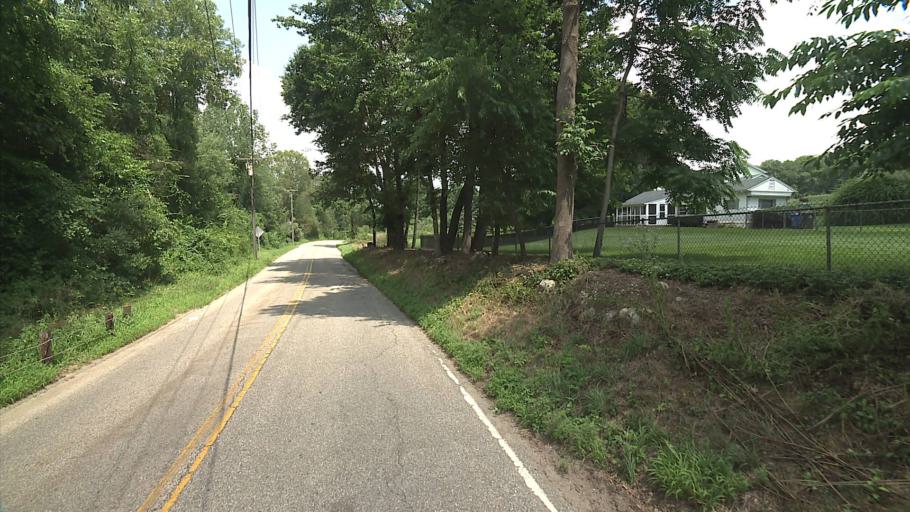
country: US
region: Connecticut
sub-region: New London County
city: Baltic
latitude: 41.6133
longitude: -72.1234
